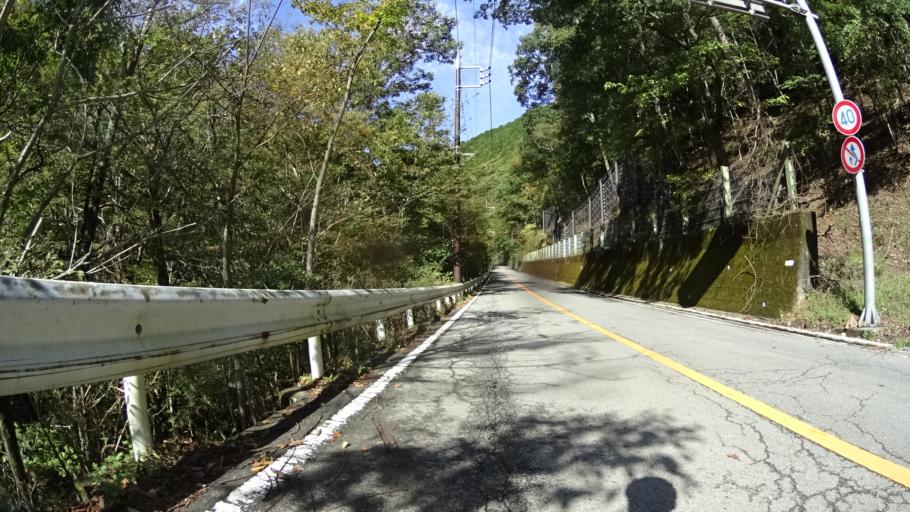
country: JP
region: Yamanashi
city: Enzan
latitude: 35.8049
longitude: 138.8421
